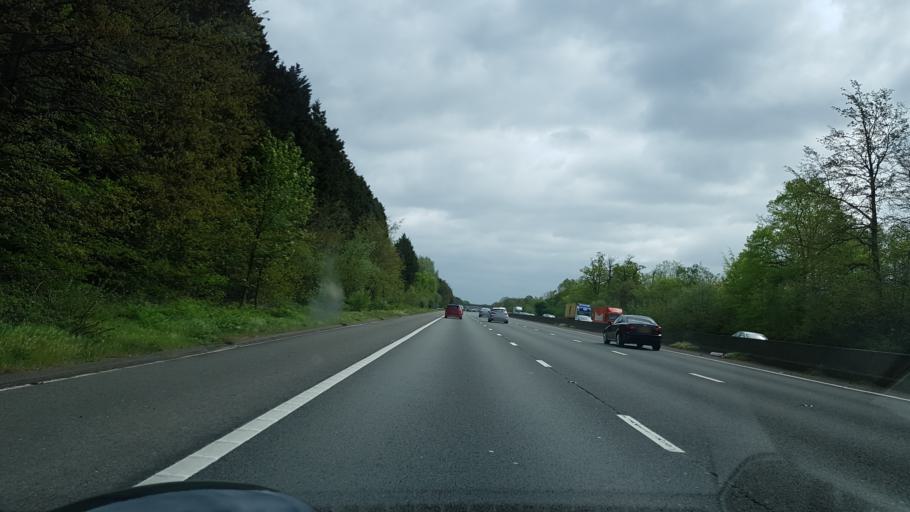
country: GB
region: England
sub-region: Hampshire
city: Fleet
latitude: 51.2991
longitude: -0.8335
